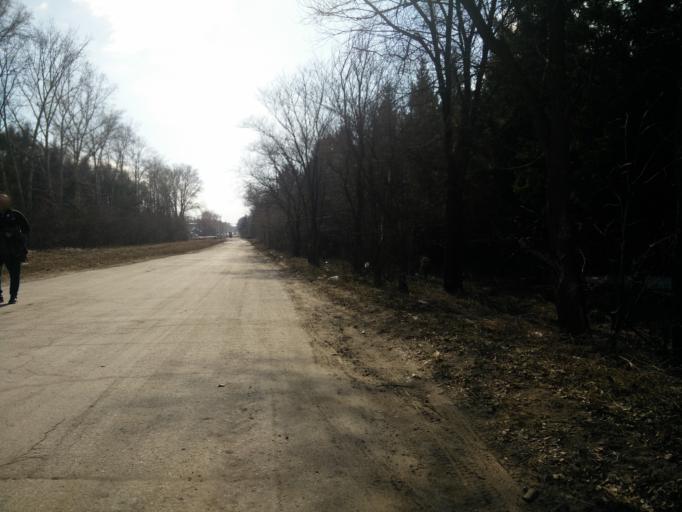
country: RU
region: Novosibirsk
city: Berdsk
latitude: 54.7605
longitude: 83.0698
